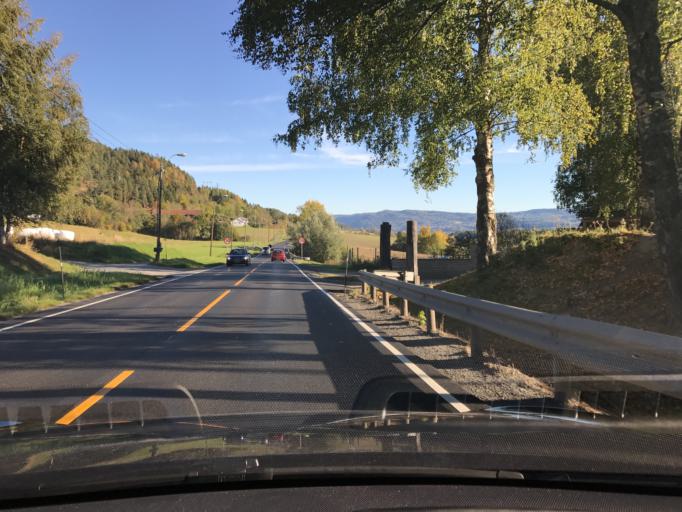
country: NO
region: Buskerud
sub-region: Ovre Eiker
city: Hokksund
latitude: 59.7762
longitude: 9.9293
